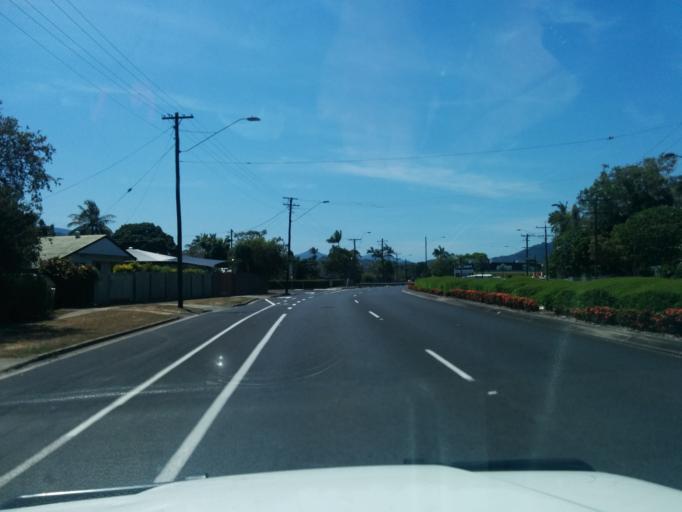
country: AU
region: Queensland
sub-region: Cairns
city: Woree
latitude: -16.9350
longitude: 145.7437
